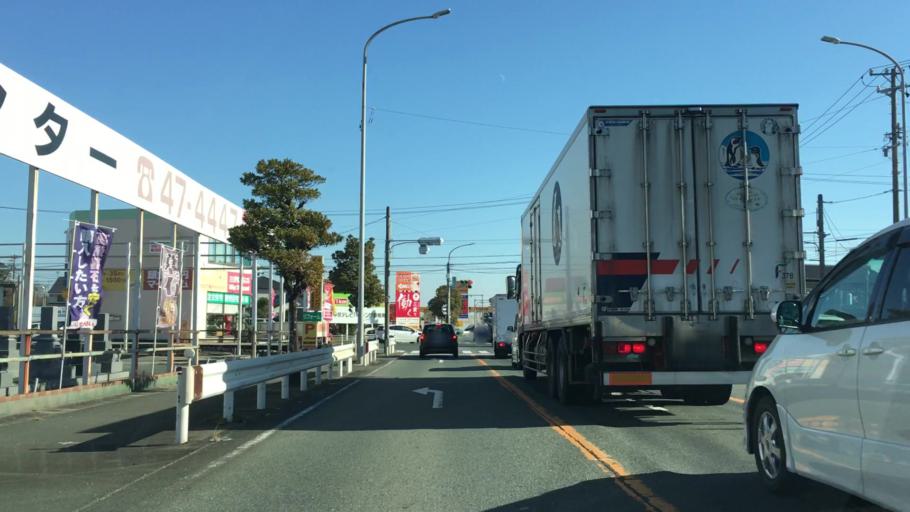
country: JP
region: Aichi
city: Toyohashi
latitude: 34.7271
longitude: 137.3558
